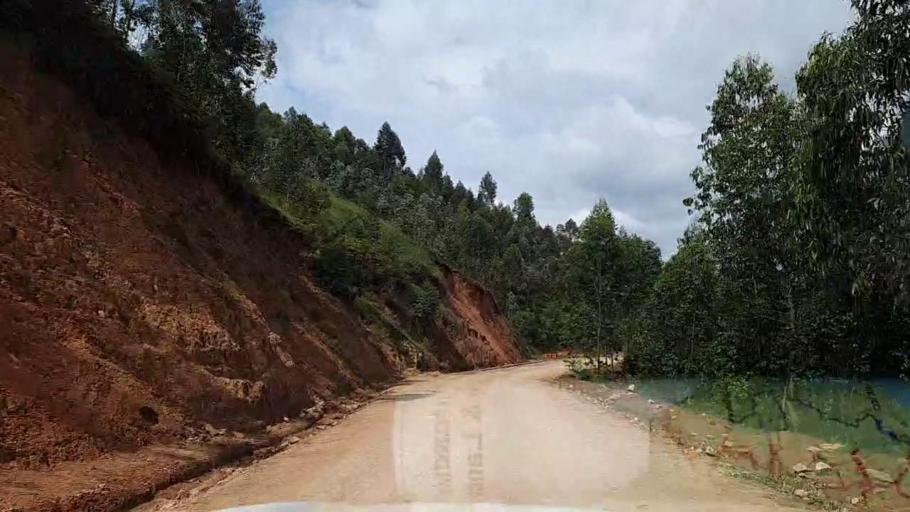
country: RW
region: Southern Province
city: Nzega
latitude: -2.3380
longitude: 29.4400
